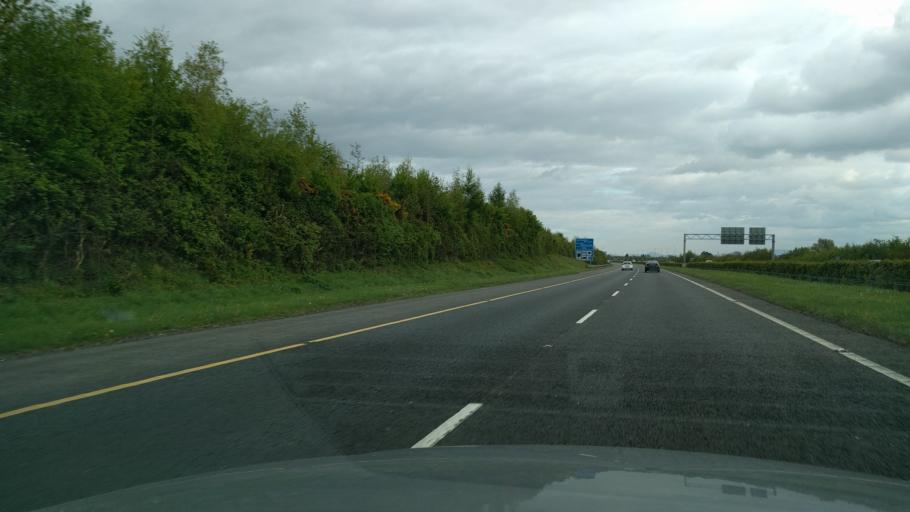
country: IE
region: Leinster
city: Balrothery
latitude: 53.5486
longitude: -6.2151
